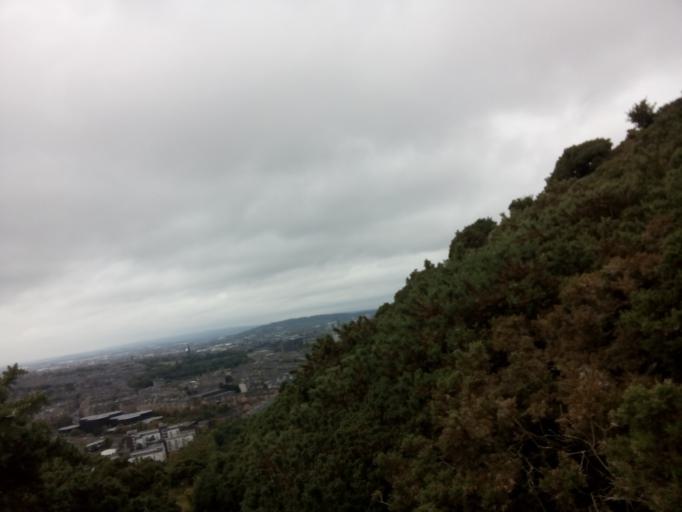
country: GB
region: Scotland
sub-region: West Lothian
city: Seafield
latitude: 55.9412
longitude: -3.1621
